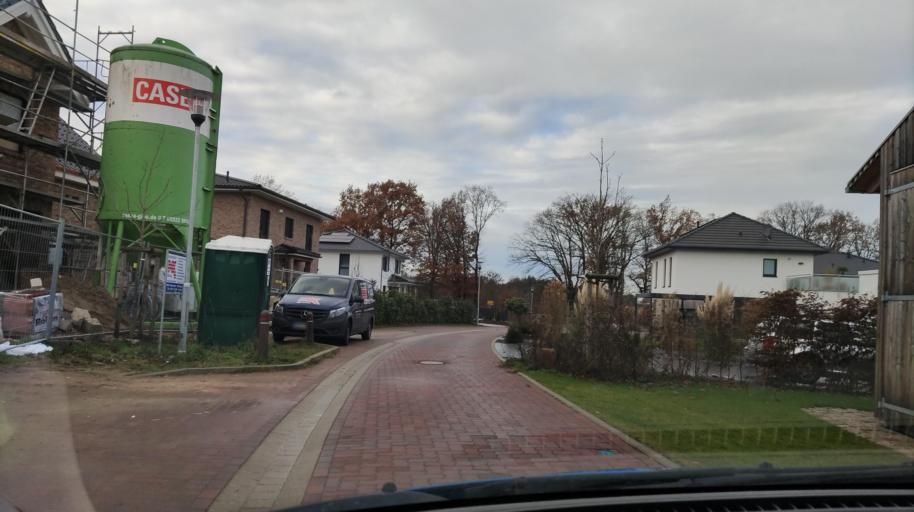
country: DE
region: Lower Saxony
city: Adendorf
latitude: 53.2926
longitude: 10.4508
